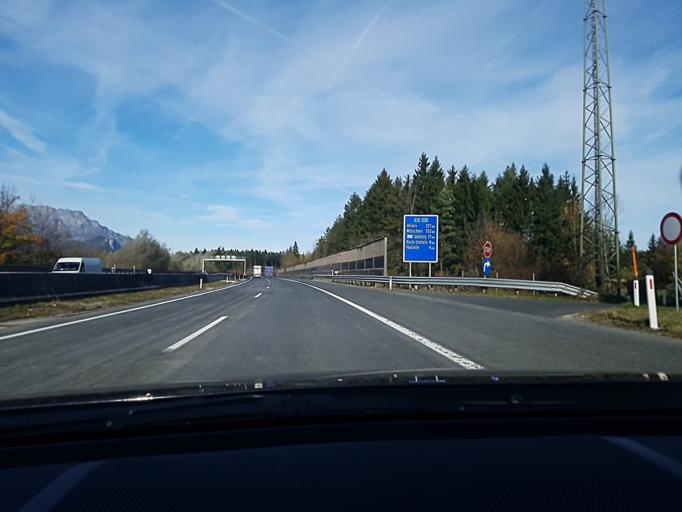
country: AT
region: Salzburg
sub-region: Politischer Bezirk Hallein
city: Adnet
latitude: 47.6561
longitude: 13.1347
